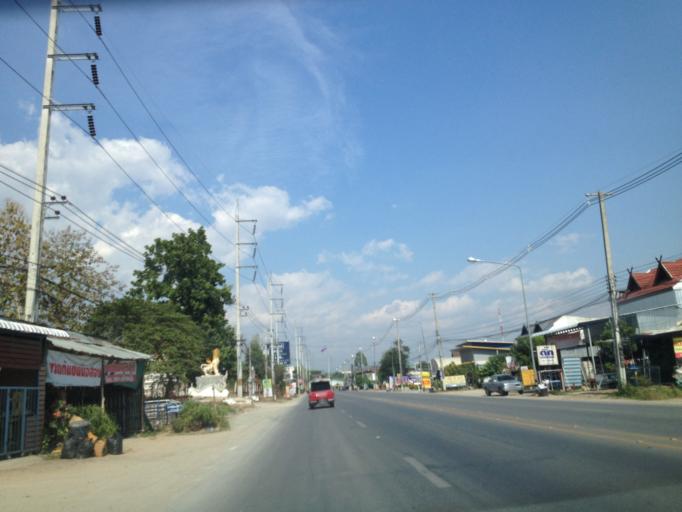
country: TH
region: Chiang Mai
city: Chom Thong
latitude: 18.4111
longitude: 98.6742
